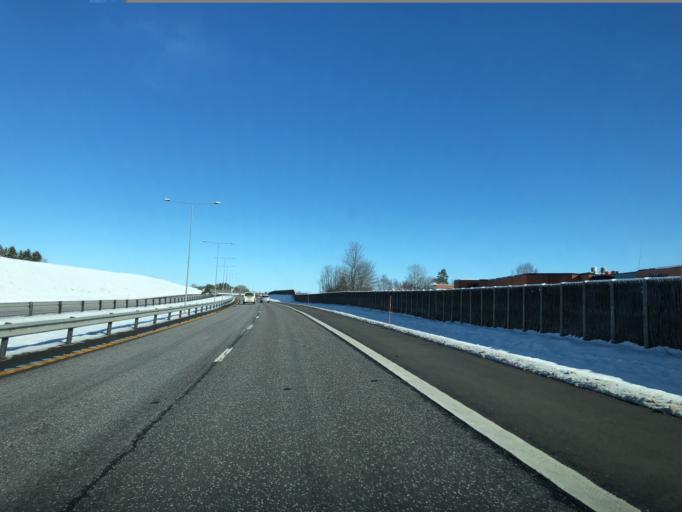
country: NO
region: Vestfold
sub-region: Sandefjord
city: Sandefjord
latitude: 59.1310
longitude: 10.1515
